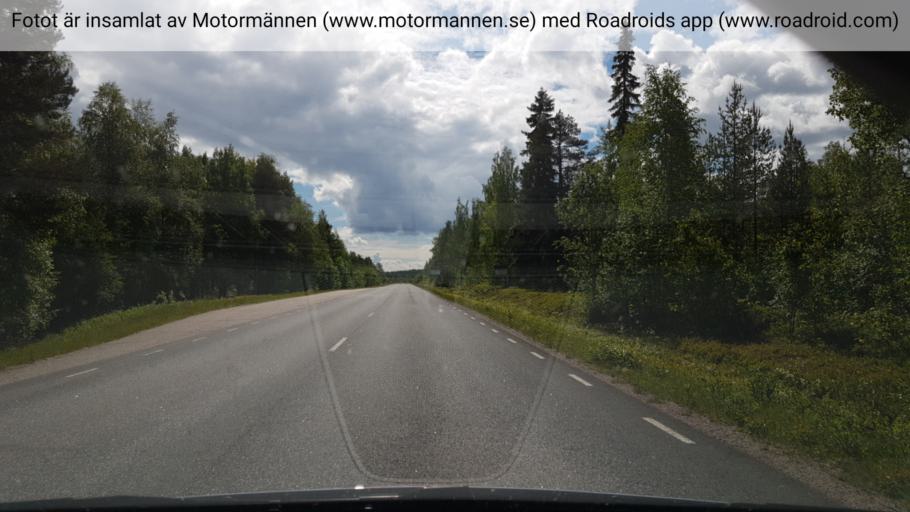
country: FI
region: Lapland
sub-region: Torniolaakso
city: Ylitornio
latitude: 66.3099
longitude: 23.6226
